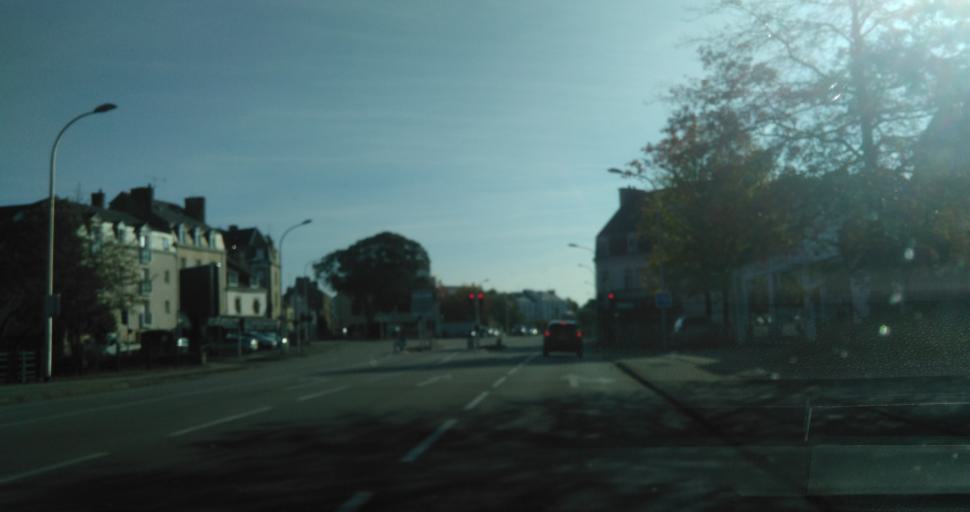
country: FR
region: Brittany
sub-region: Departement du Morbihan
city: Vannes
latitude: 47.6589
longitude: -2.7493
